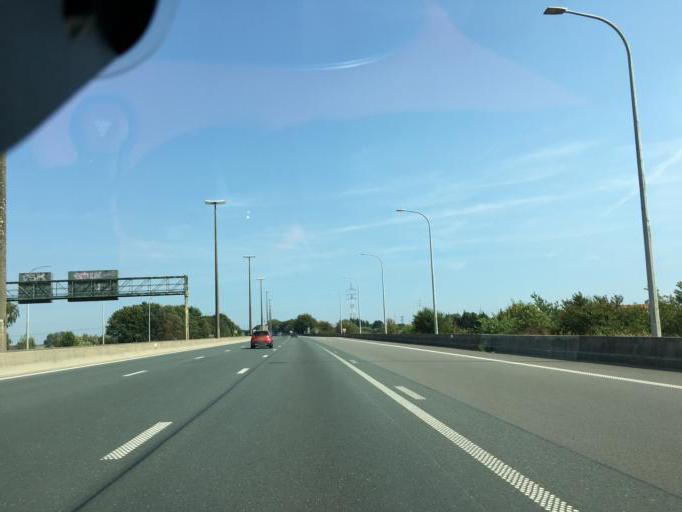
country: BE
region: Wallonia
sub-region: Province du Hainaut
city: Fleurus
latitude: 50.4702
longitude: 4.5059
